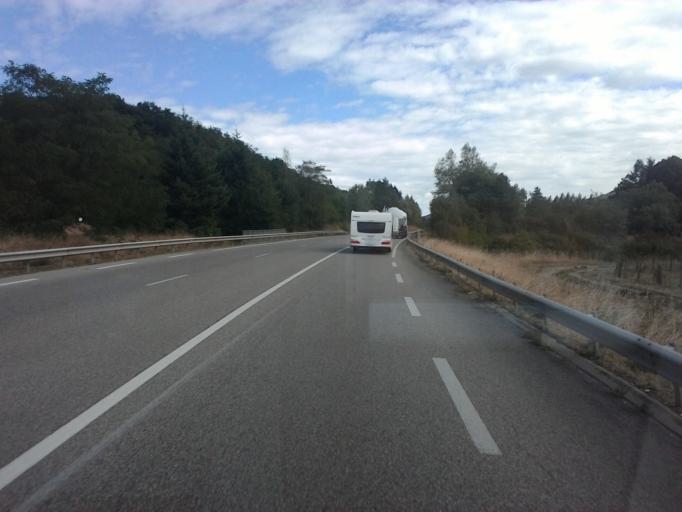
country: FR
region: Rhone-Alpes
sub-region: Departement de l'Ain
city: Lagnieu
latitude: 45.8910
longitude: 5.3372
